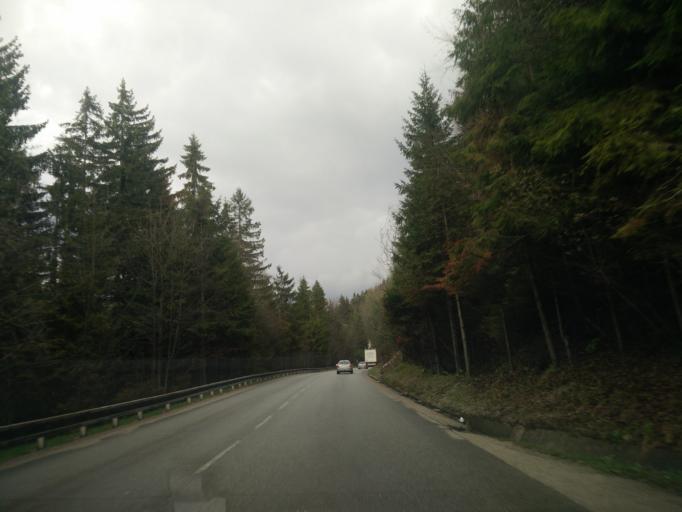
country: SK
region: Banskobystricky
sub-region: Okres Ziar nad Hronom
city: Kremnica
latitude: 48.8365
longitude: 18.9657
